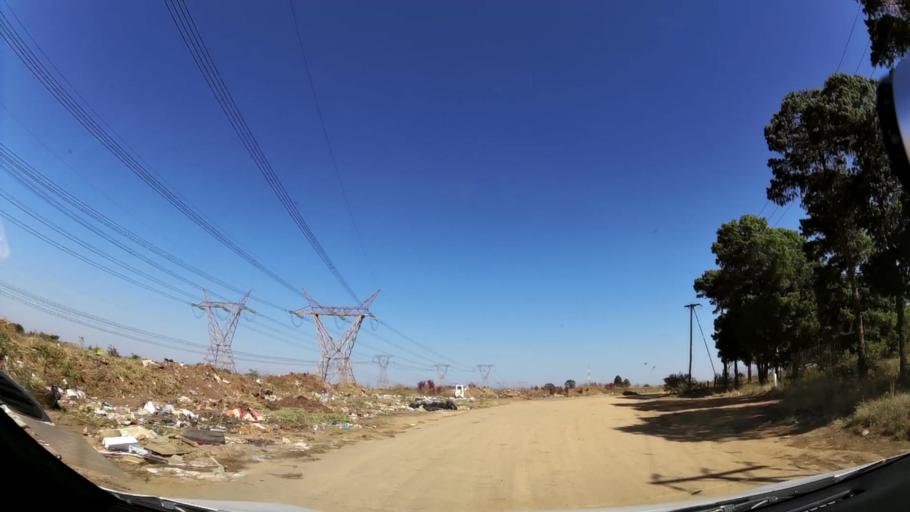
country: ZA
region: Gauteng
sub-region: City of Johannesburg Metropolitan Municipality
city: Diepsloot
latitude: -25.9038
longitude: 28.0852
